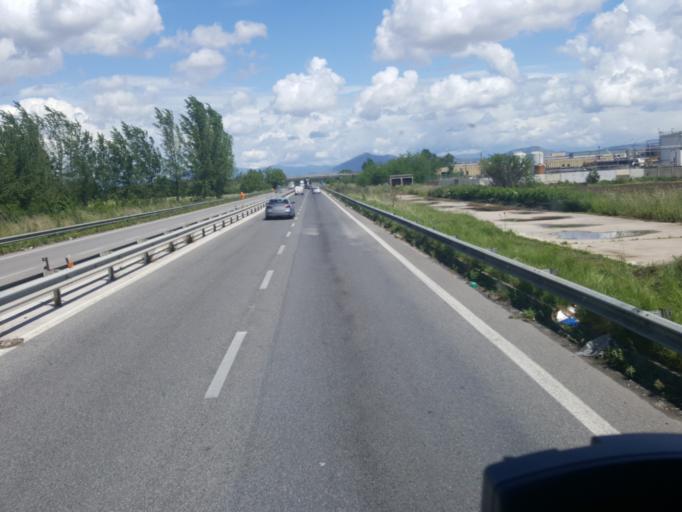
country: IT
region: Campania
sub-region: Provincia di Napoli
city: Pascarola
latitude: 40.9825
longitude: 14.2934
